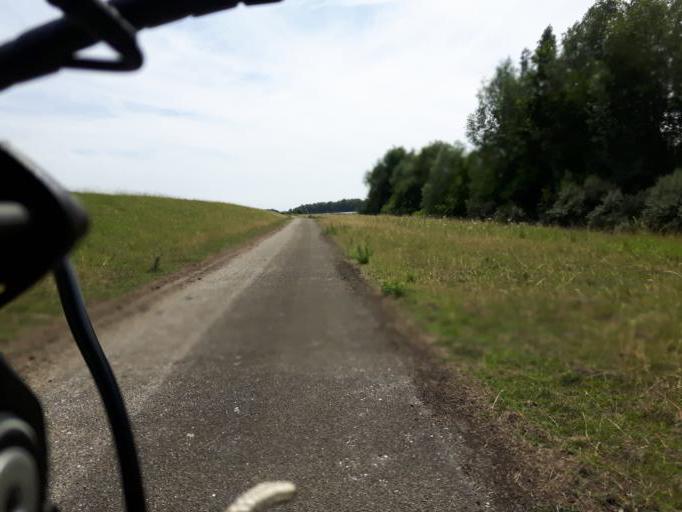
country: NL
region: North Brabant
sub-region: Gemeente Steenbergen
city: Nieuw-Vossemeer
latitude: 51.6039
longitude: 4.1922
